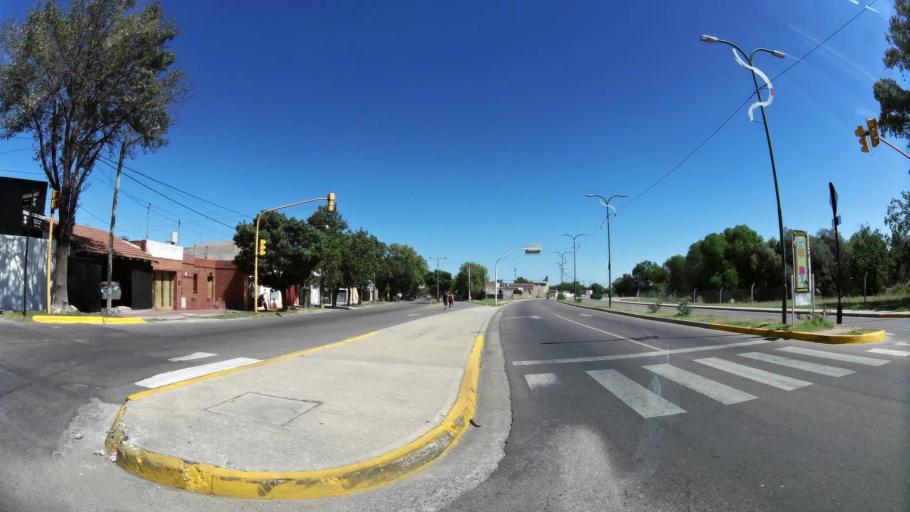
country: AR
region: San Luis
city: San Luis
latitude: -33.2898
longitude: -66.3295
